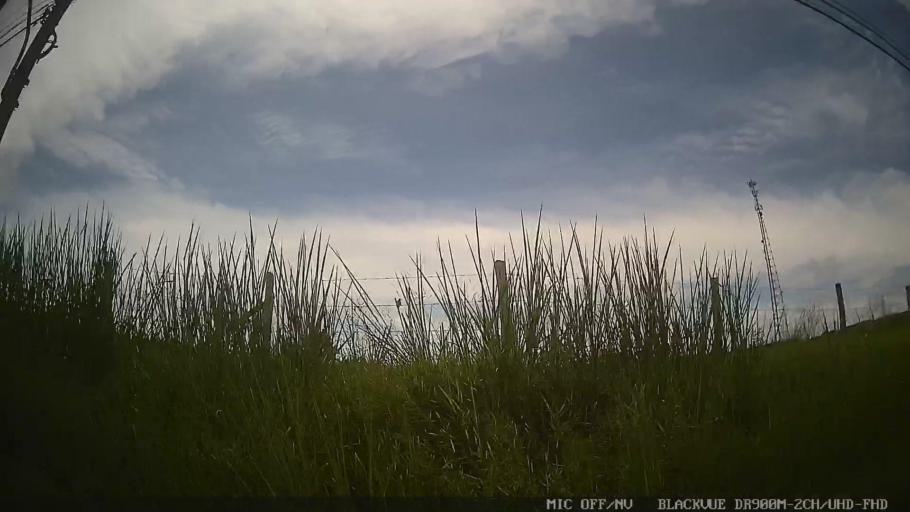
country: BR
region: Sao Paulo
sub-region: Santa Isabel
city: Santa Isabel
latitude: -23.3918
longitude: -46.1716
